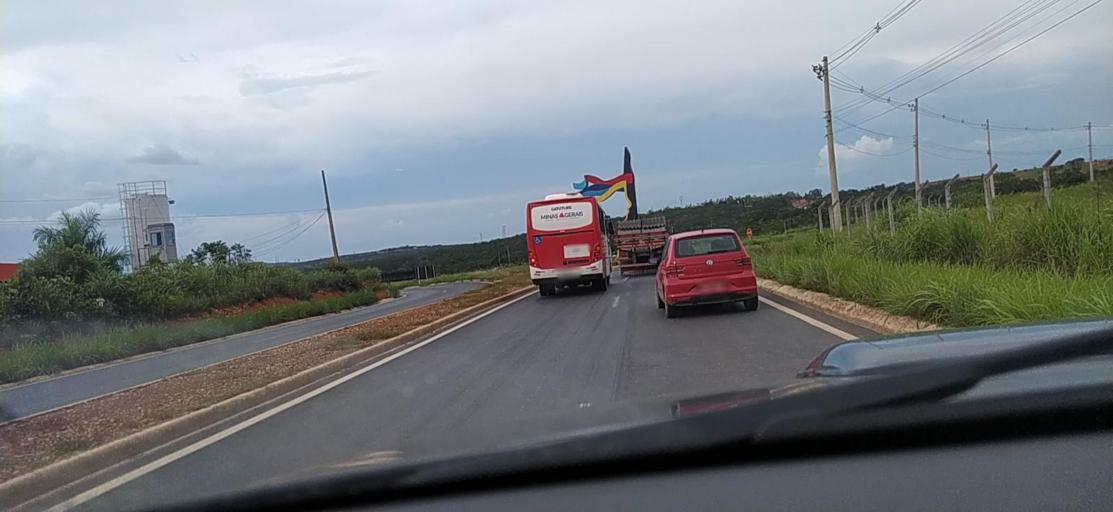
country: BR
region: Minas Gerais
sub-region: Montes Claros
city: Montes Claros
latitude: -16.6775
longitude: -43.8010
